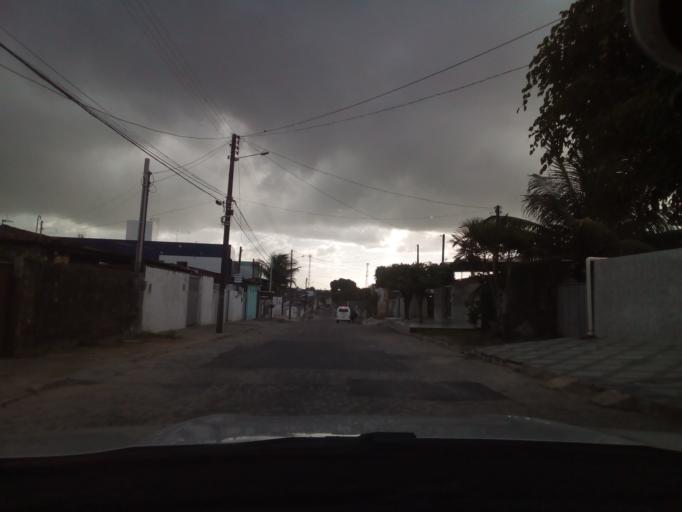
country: BR
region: Paraiba
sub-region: Bayeux
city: Bayeux
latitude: -7.1704
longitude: -34.8904
